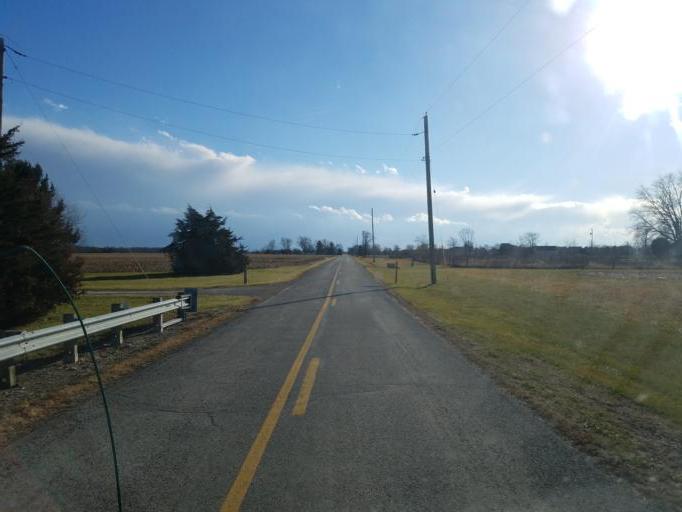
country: US
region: Ohio
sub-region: Marion County
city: Prospect
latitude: 40.4144
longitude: -83.1434
